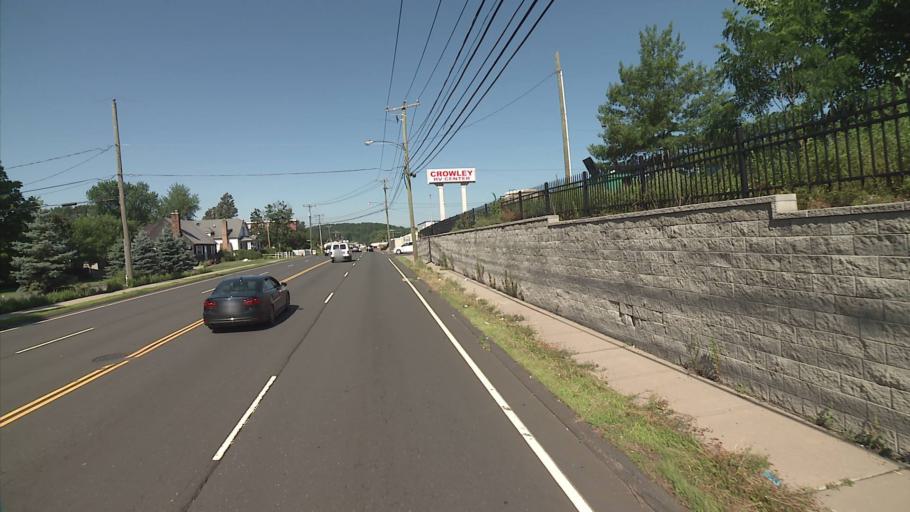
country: US
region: Connecticut
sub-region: Hartford County
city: Bristol
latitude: 41.6691
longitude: -72.9103
